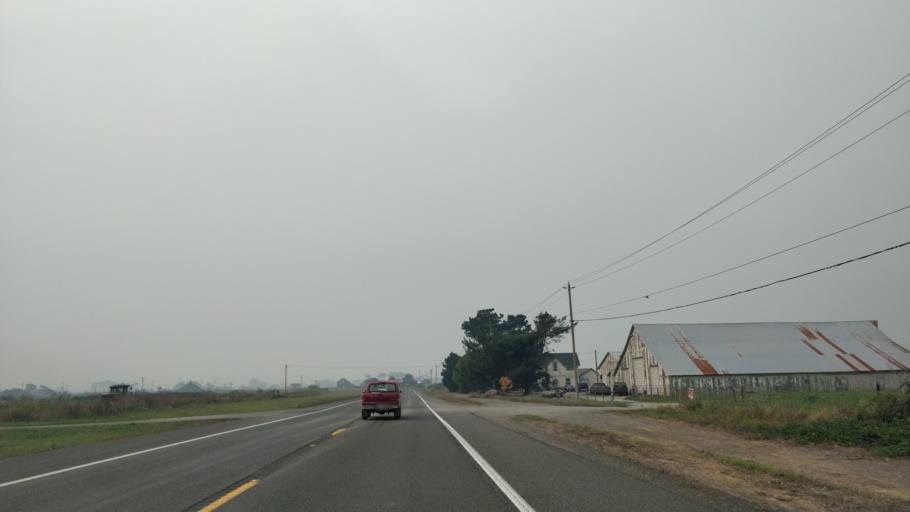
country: US
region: California
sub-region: Humboldt County
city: Ferndale
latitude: 40.5990
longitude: -124.2225
